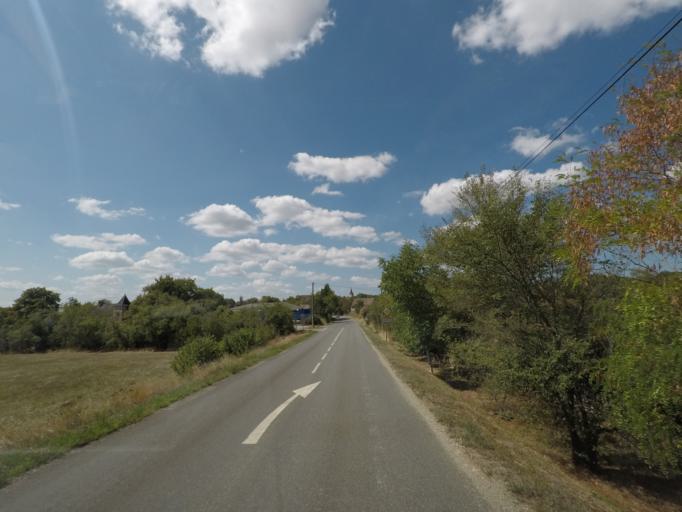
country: FR
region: Midi-Pyrenees
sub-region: Departement du Lot
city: Lacapelle-Marival
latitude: 44.6269
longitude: 1.8263
